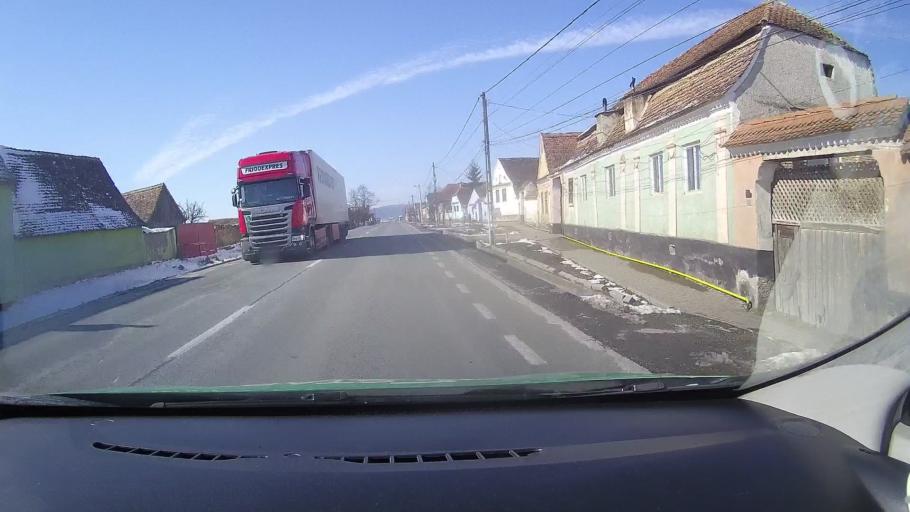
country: RO
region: Brasov
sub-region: Comuna Bunesti
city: Bunesti
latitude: 46.1079
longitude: 25.0574
